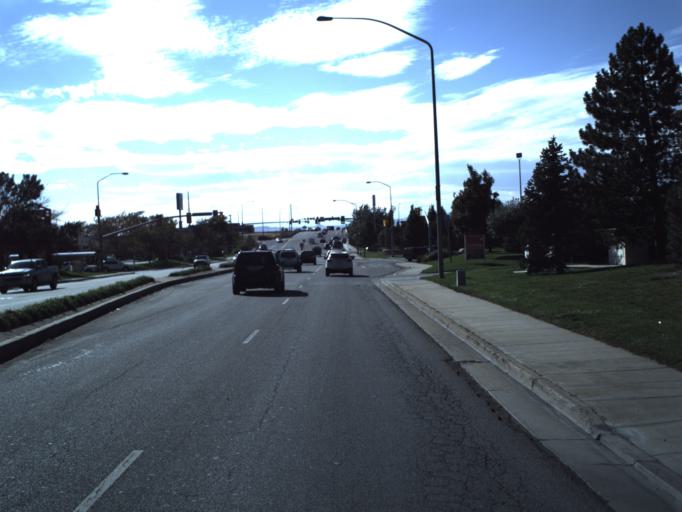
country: US
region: Utah
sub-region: Davis County
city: Centerville
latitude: 40.9216
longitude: -111.8863
